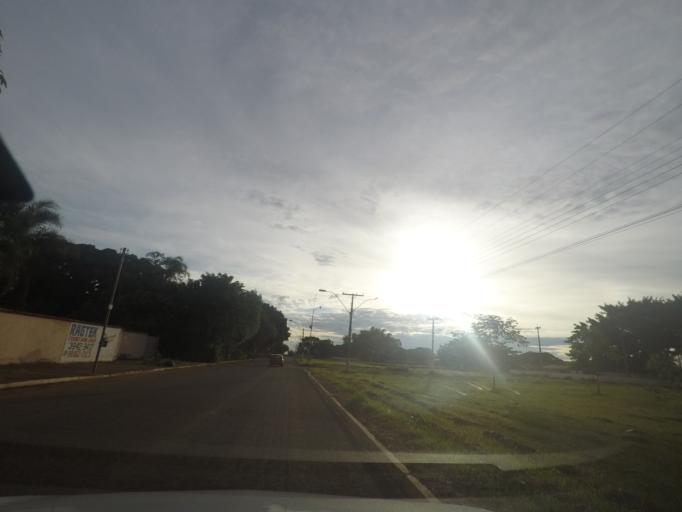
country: BR
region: Goias
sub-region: Trindade
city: Trindade
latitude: -16.7199
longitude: -49.4333
